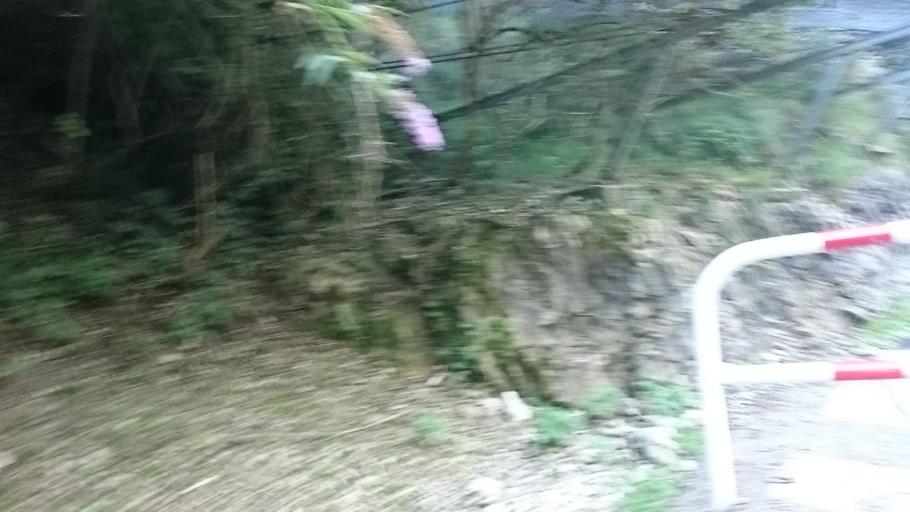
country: IT
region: Veneto
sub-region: Provincia di Vicenza
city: Enego
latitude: 45.9494
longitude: 11.7239
